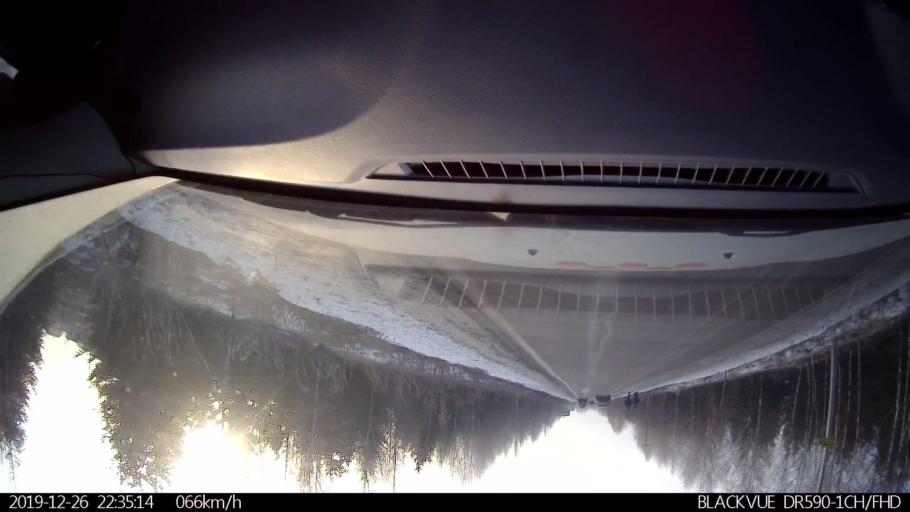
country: RU
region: Nizjnij Novgorod
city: Burevestnik
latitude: 56.1492
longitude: 43.7173
